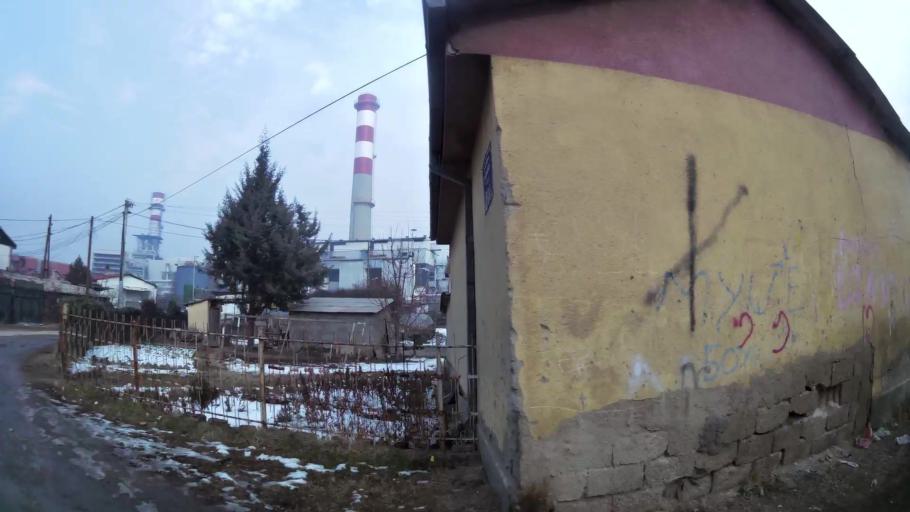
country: MK
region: Karpos
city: Skopje
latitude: 41.9924
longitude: 21.4535
